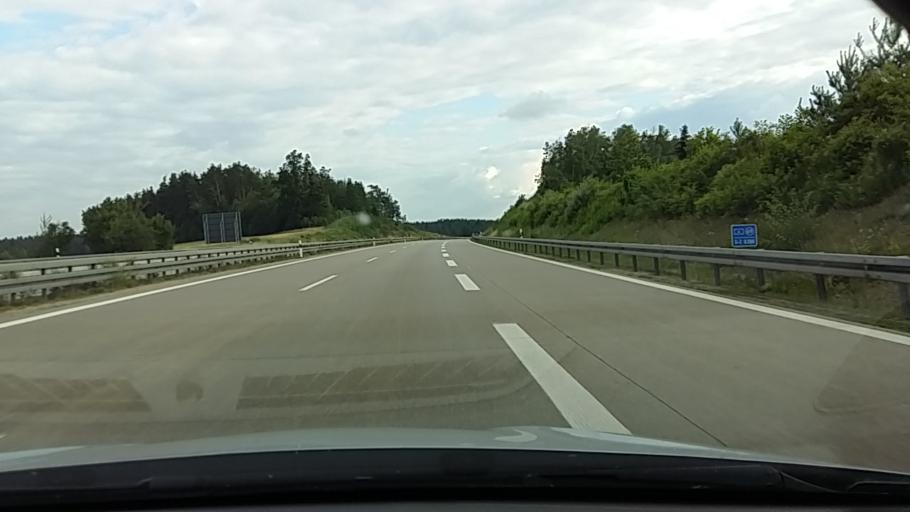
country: DE
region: Bavaria
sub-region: Upper Palatinate
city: Nabburg
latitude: 49.4650
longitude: 12.1349
